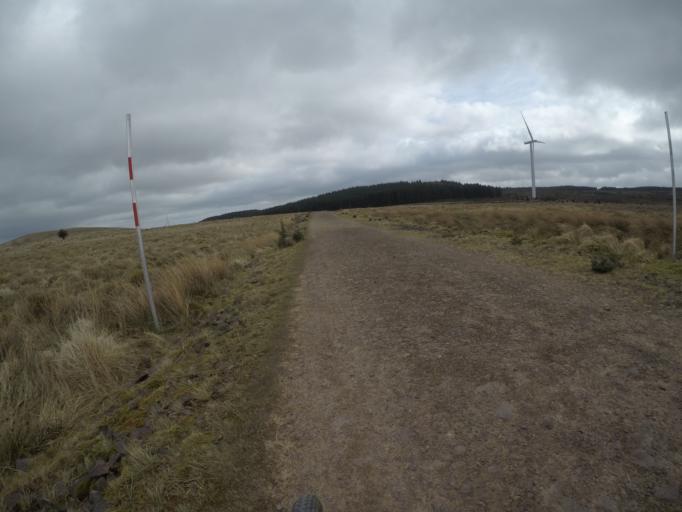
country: GB
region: Scotland
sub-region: East Renfrewshire
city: Eaglesham
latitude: 55.7079
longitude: -4.2998
